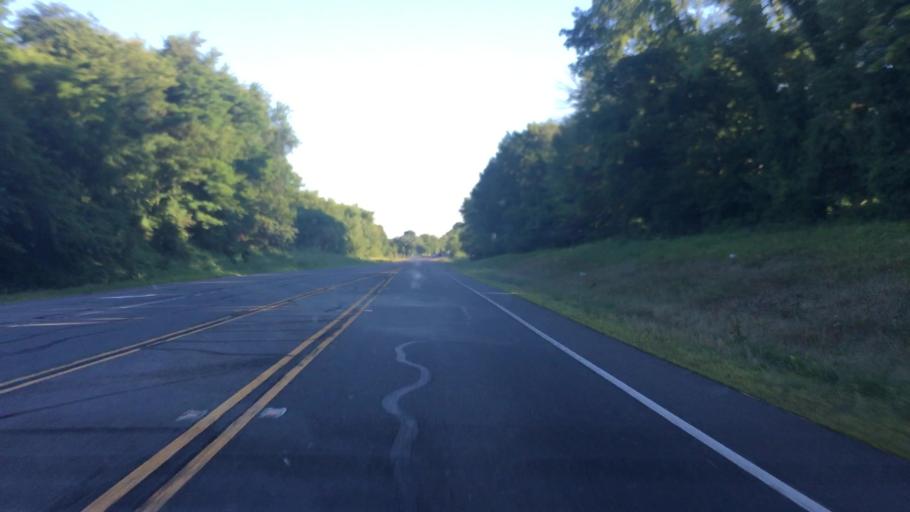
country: US
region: Virginia
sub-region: Loudoun County
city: Brambleton
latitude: 38.9898
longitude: -77.6183
